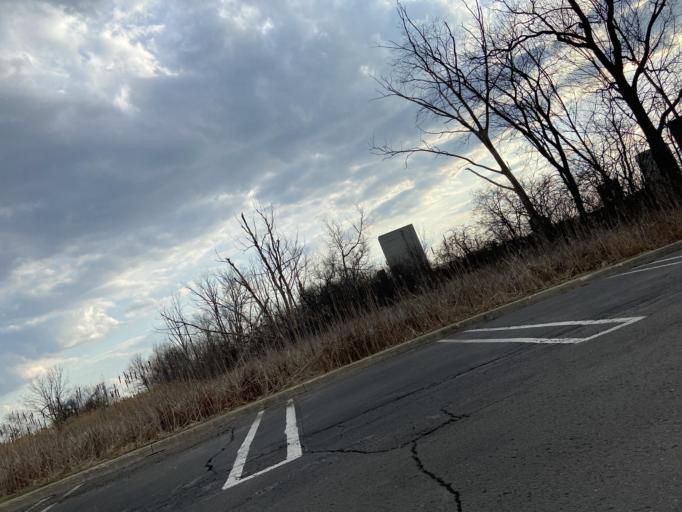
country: US
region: Michigan
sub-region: Oakland County
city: Southfield
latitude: 42.4825
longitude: -83.2513
